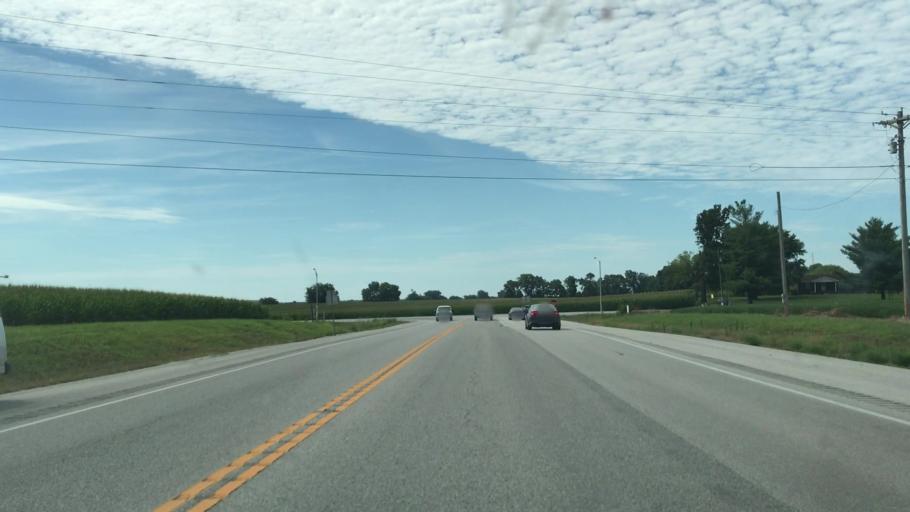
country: US
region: Kentucky
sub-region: Edmonson County
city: Brownsville
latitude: 37.0866
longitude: -86.2293
